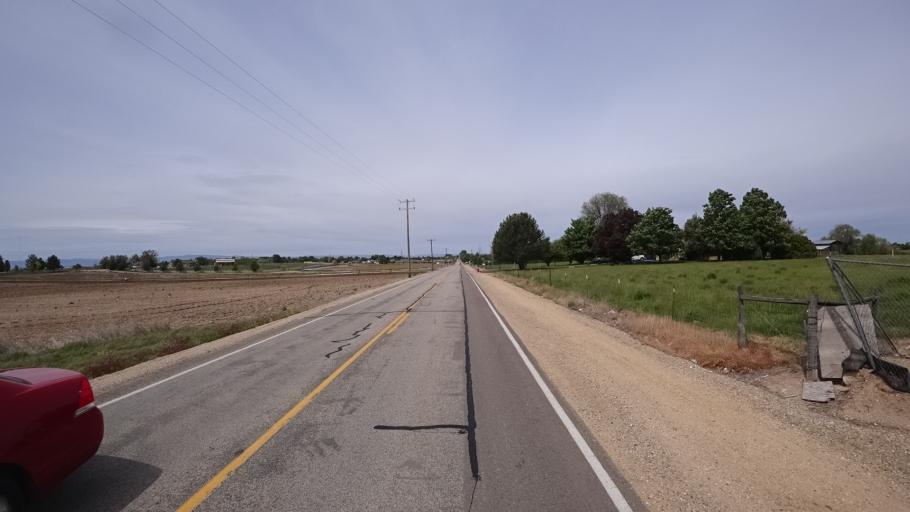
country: US
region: Idaho
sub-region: Ada County
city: Meridian
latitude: 43.5609
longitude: -116.4018
